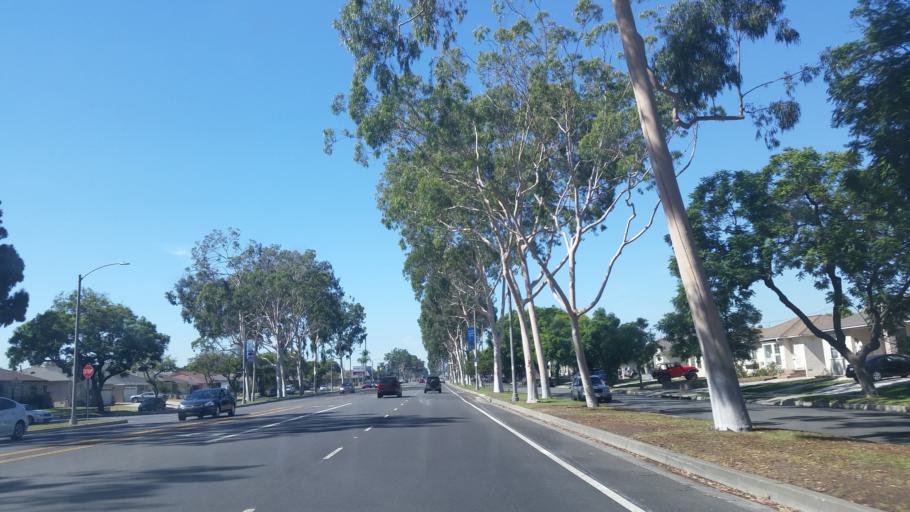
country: US
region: California
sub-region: Los Angeles County
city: Lakewood
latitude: 33.8471
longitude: -118.1123
